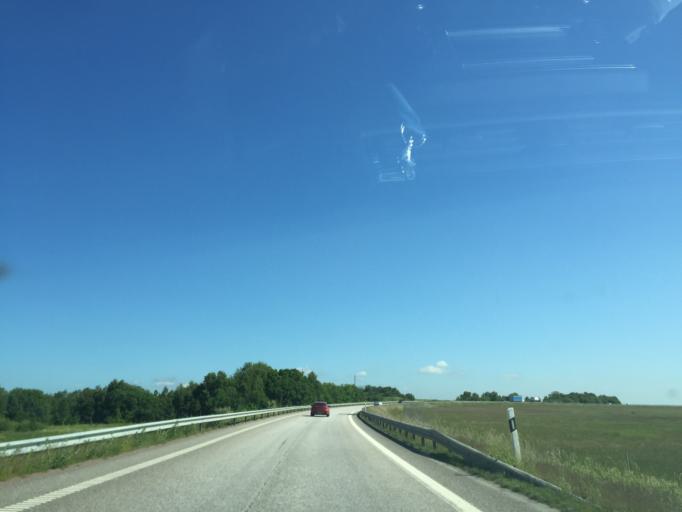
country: SE
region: Skane
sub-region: Helsingborg
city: Odakra
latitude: 56.0844
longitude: 12.7804
